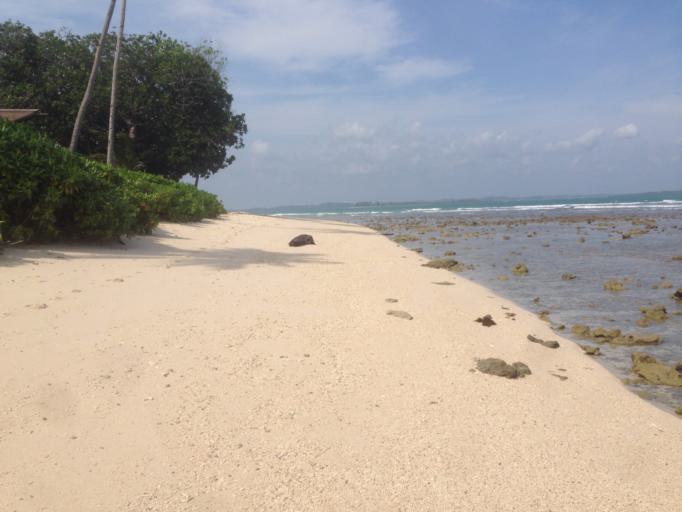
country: ID
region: Riau Islands
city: Kijang
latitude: 1.0532
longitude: 104.7085
